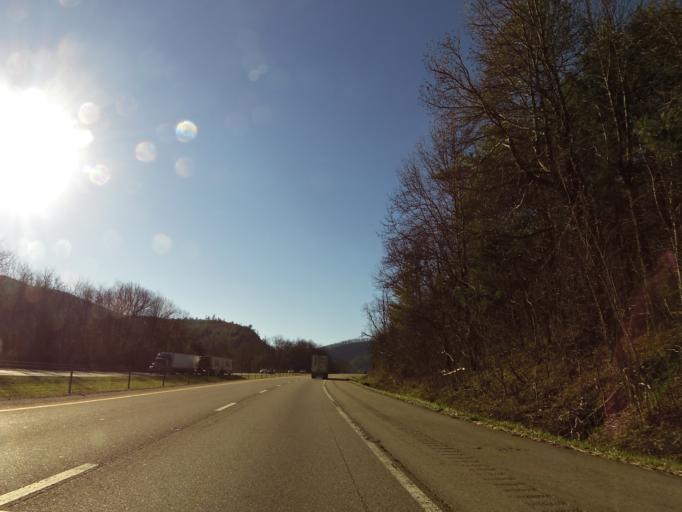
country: US
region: Tennessee
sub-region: Cocke County
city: Newport
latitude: 35.8378
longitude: -83.1810
